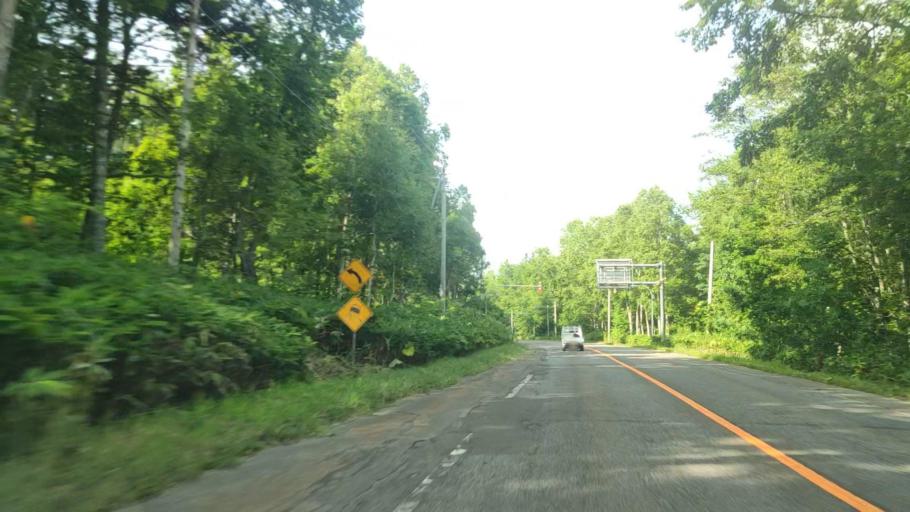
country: JP
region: Hokkaido
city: Nayoro
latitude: 44.3886
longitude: 142.3977
